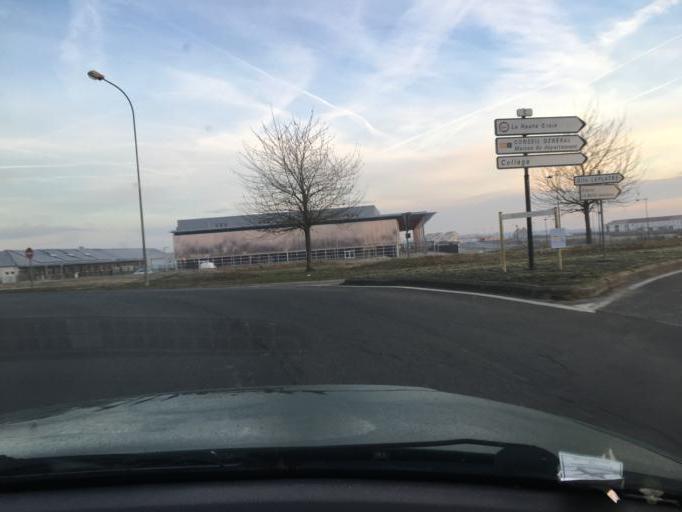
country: FR
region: Centre
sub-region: Departement du Loiret
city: Meung-sur-Loire
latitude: 47.8315
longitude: 1.6787
